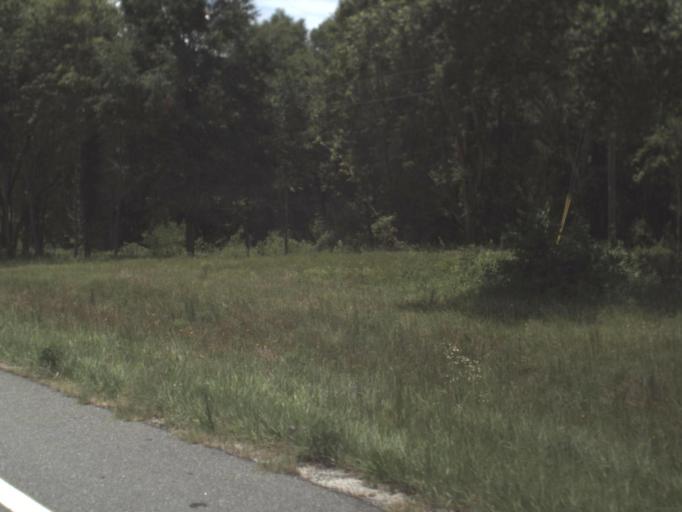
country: US
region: Florida
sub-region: Columbia County
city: Five Points
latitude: 30.3102
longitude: -82.7128
